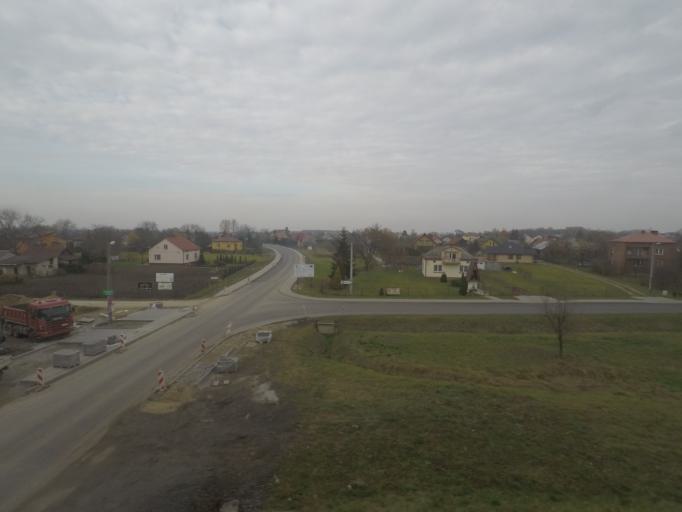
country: PL
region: Subcarpathian Voivodeship
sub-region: Powiat przemyski
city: Medyka
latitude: 49.8011
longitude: 22.9251
